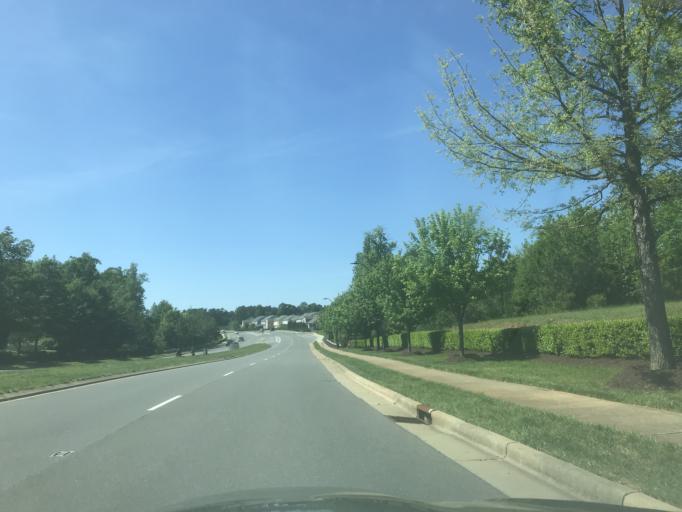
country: US
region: North Carolina
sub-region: Wake County
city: Raleigh
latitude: 35.7331
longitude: -78.6583
